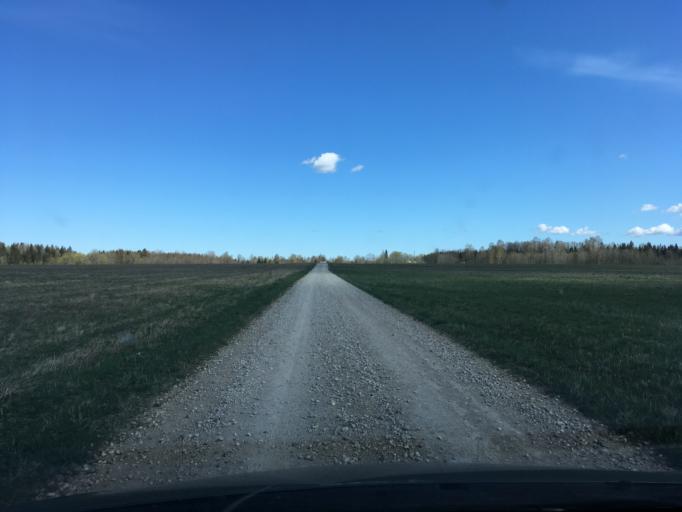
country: EE
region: Harju
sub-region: Raasiku vald
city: Raasiku
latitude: 59.2196
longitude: 25.2109
